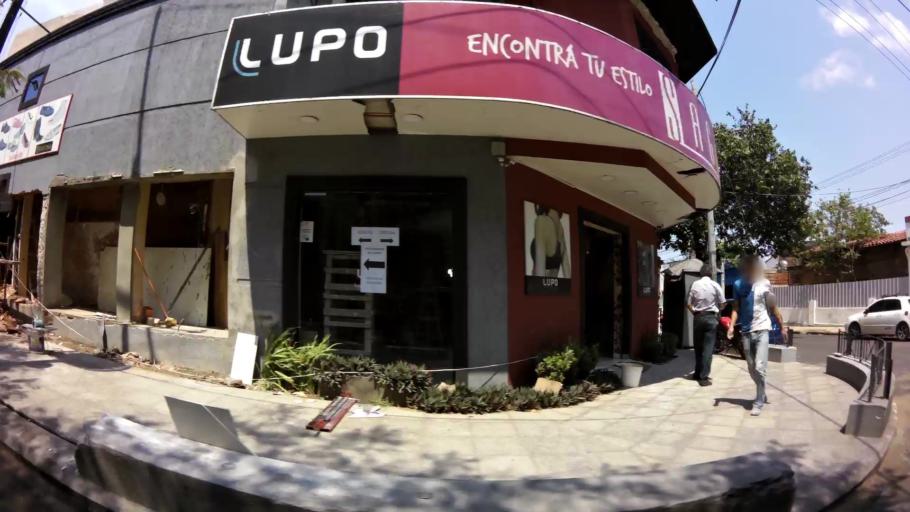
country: PY
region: Asuncion
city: Asuncion
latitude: -25.2954
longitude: -57.6387
